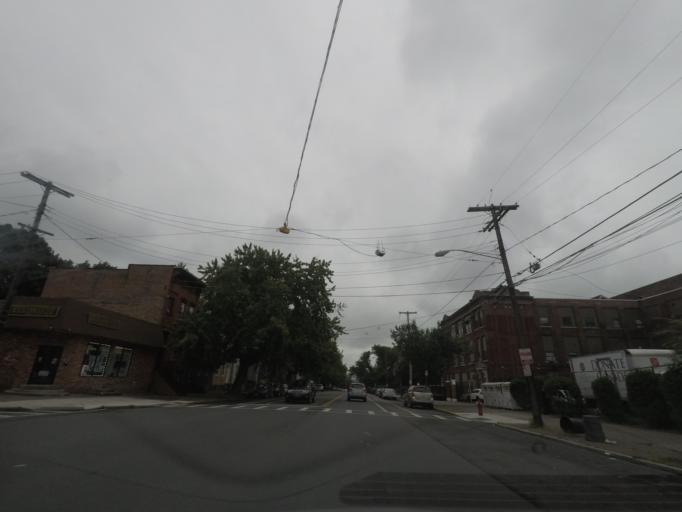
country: US
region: New York
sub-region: Albany County
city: Albany
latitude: 42.6638
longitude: -73.7665
